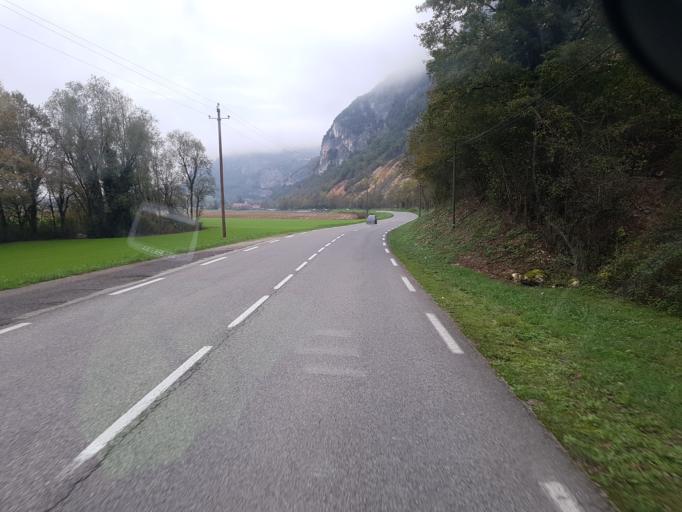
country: FR
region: Rhone-Alpes
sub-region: Departement de la Savoie
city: Yenne
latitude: 45.6944
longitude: 5.7155
